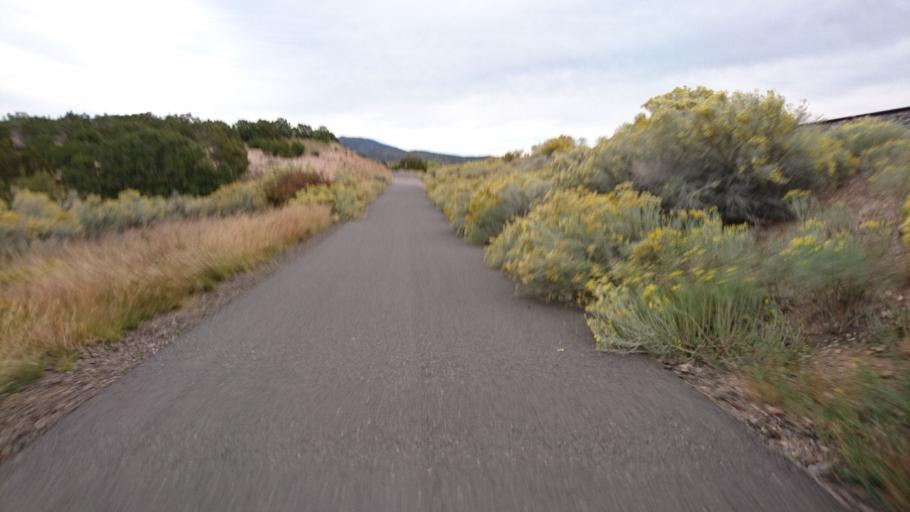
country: US
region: New Mexico
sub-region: Santa Fe County
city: Santa Fe
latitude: 35.6503
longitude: -105.9611
